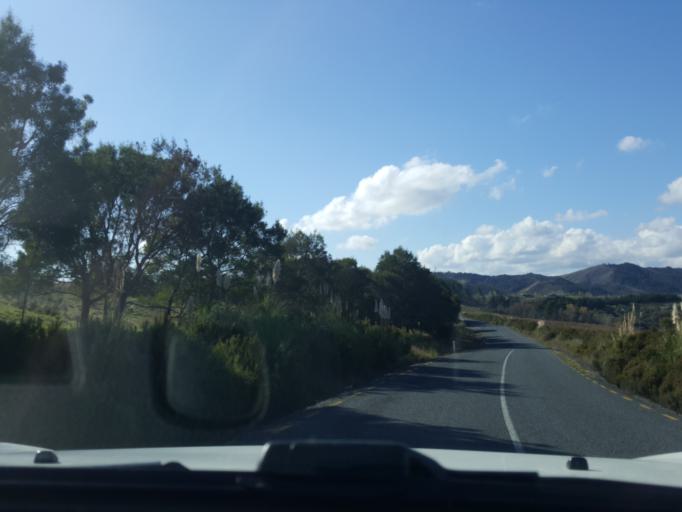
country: NZ
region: Waikato
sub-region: Waikato District
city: Ngaruawahia
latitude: -37.5379
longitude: 175.1752
